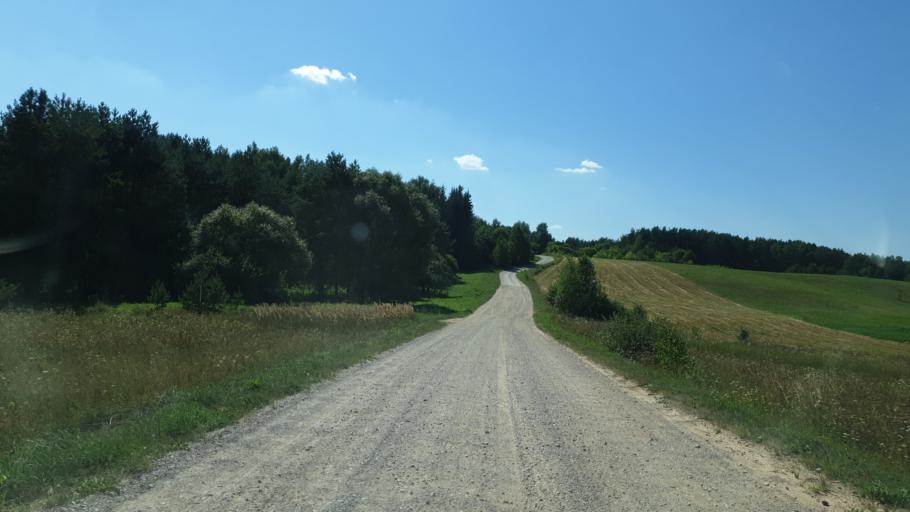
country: LT
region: Vilnius County
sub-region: Vilniaus Rajonas
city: Vievis
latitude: 54.8924
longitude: 24.8624
